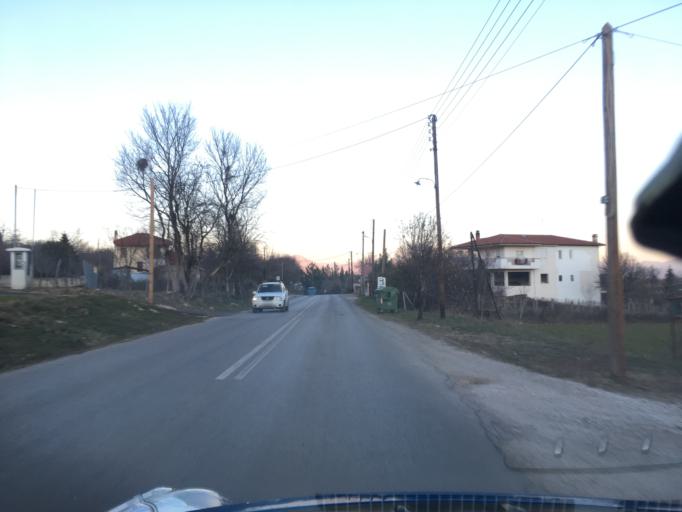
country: GR
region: West Macedonia
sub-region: Nomos Kozanis
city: Kozani
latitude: 40.2685
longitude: 21.7728
